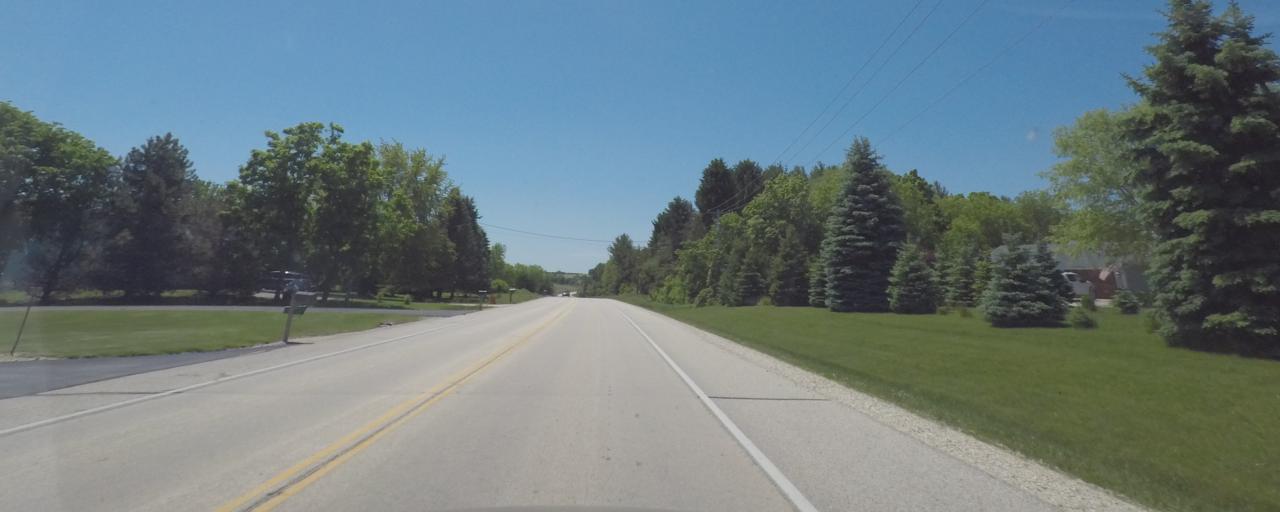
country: US
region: Wisconsin
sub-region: Ozaukee County
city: Kohler
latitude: 43.5351
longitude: -88.0930
